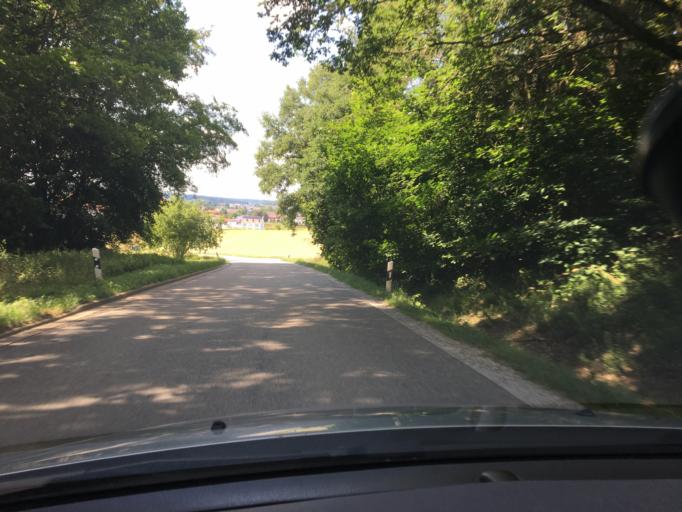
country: DE
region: Bavaria
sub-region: Lower Bavaria
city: Geisenhausen
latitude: 48.4663
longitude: 12.2691
